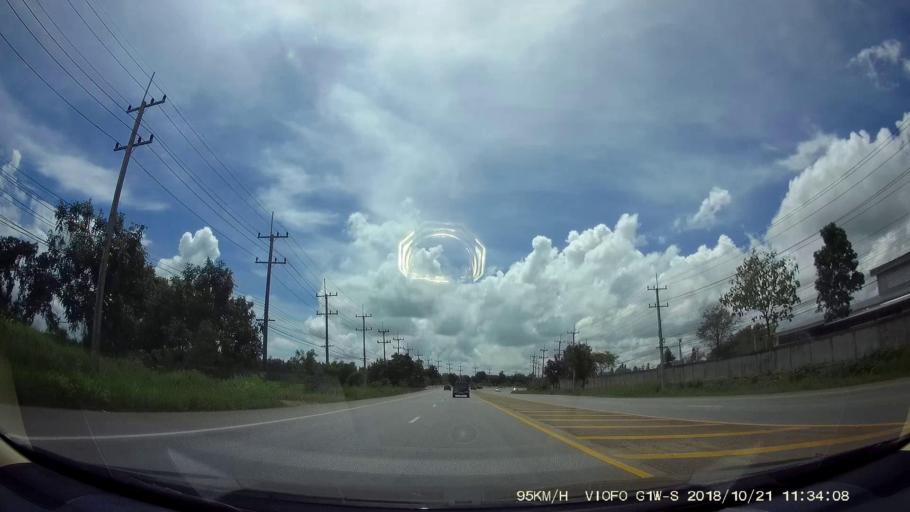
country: TH
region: Chaiyaphum
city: Chaiyaphum
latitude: 15.7357
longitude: 102.0244
